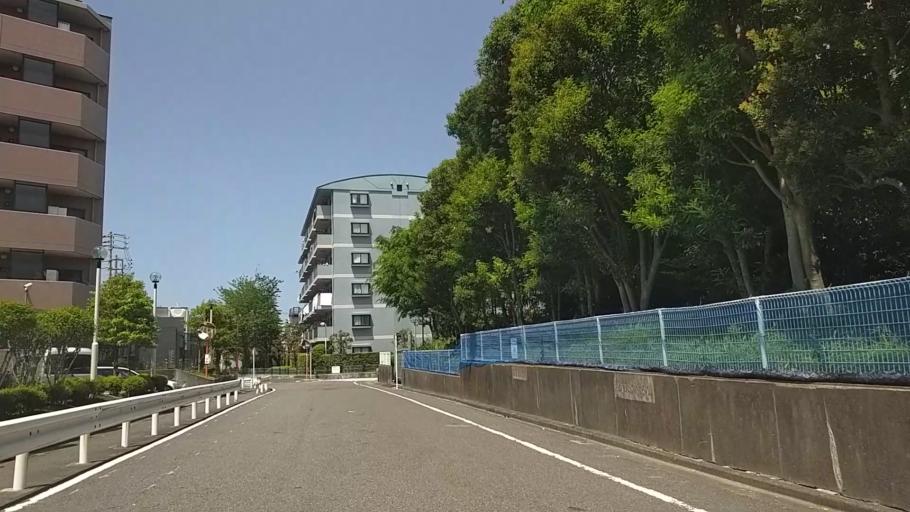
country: JP
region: Kanagawa
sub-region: Kawasaki-shi
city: Kawasaki
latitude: 35.5077
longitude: 139.7072
